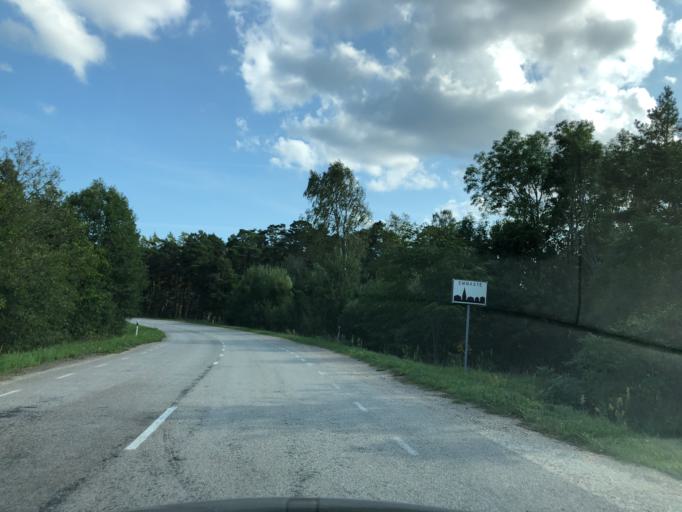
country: EE
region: Hiiumaa
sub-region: Kaerdla linn
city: Kardla
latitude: 58.7086
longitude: 22.5882
